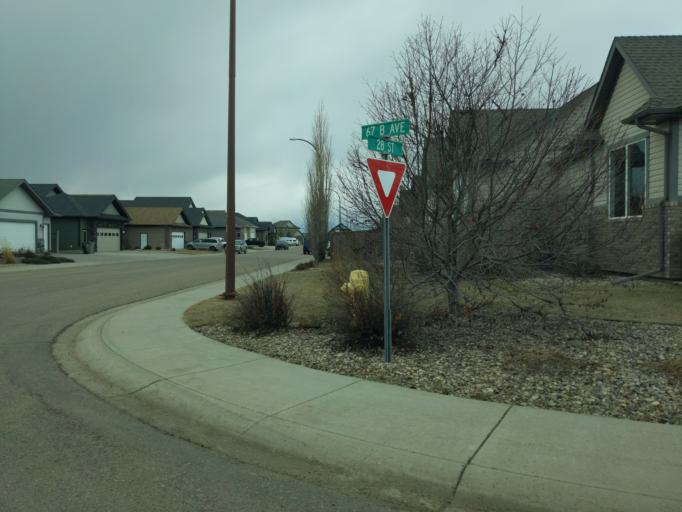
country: CA
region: Saskatchewan
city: Lloydminster
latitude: 53.2640
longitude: -110.0423
